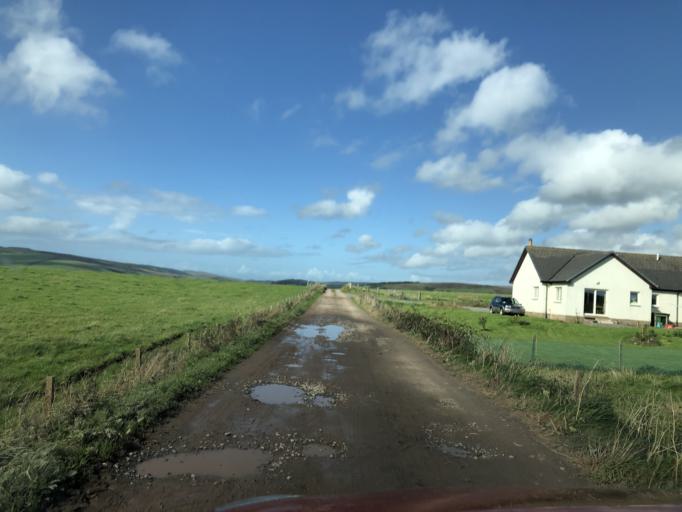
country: GB
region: Scotland
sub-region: Argyll and Bute
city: Campbeltown
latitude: 55.3138
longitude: -5.6086
